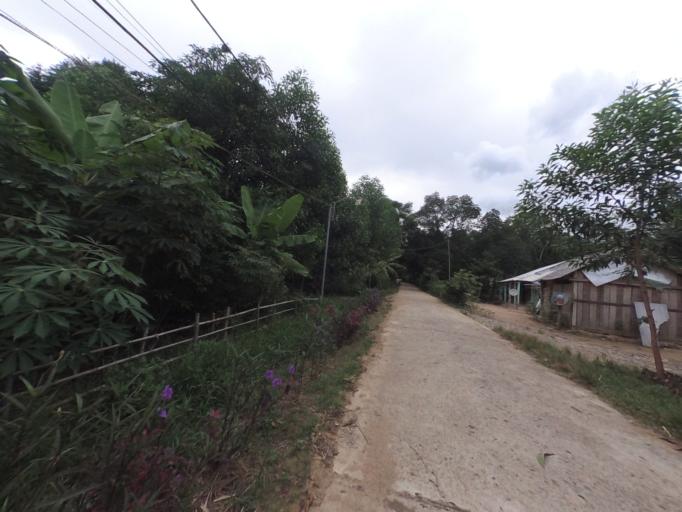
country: VN
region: Thua Thien-Hue
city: A Luoi
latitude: 16.2981
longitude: 107.3493
